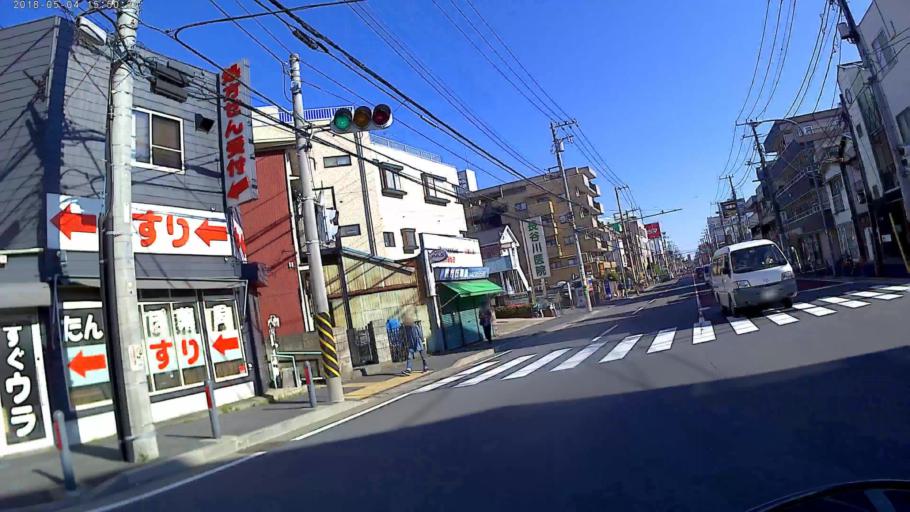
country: JP
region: Kanagawa
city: Yokohama
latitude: 35.4951
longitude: 139.6477
